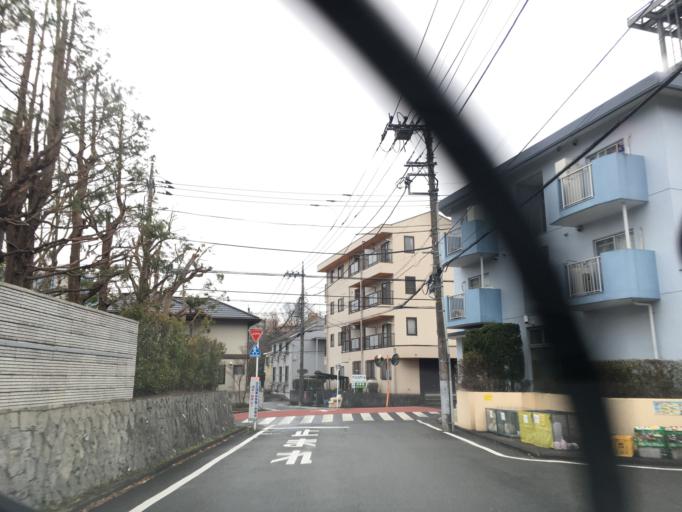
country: JP
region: Tokyo
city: Hino
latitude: 35.6246
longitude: 139.4162
